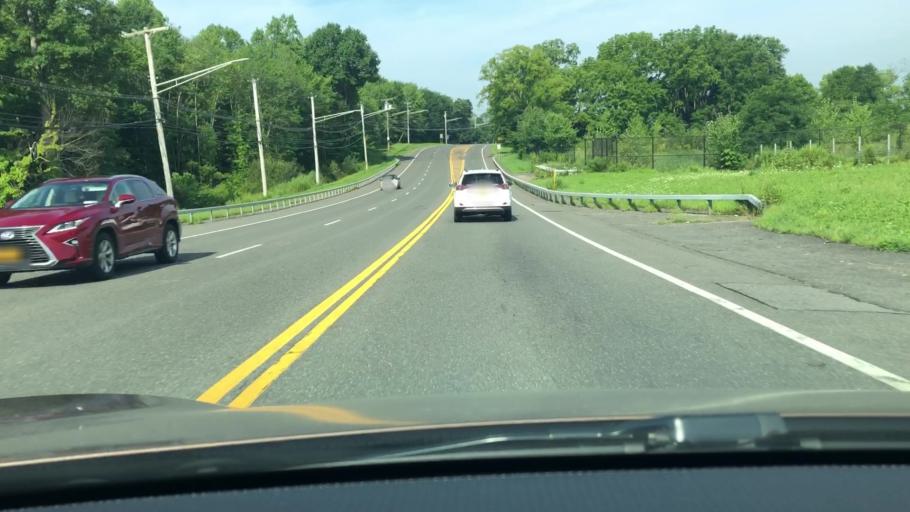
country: US
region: New York
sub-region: Westchester County
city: Elmsford
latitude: 41.0757
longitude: -73.8090
